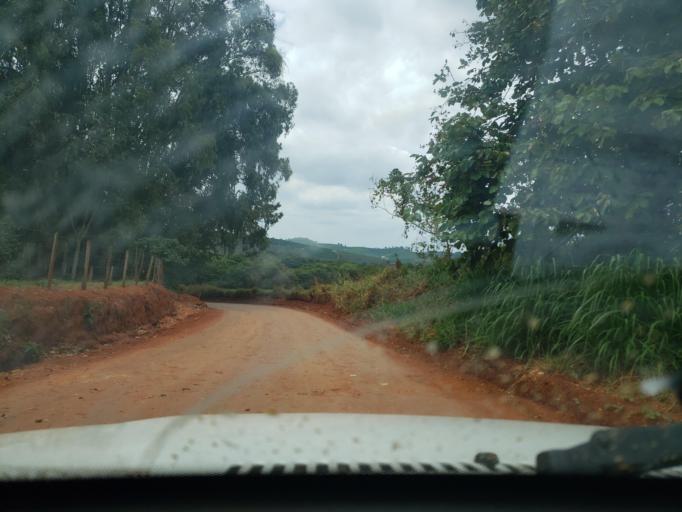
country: BR
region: Minas Gerais
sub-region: Boa Esperanca
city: Boa Esperanca
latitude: -20.9839
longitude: -45.5929
